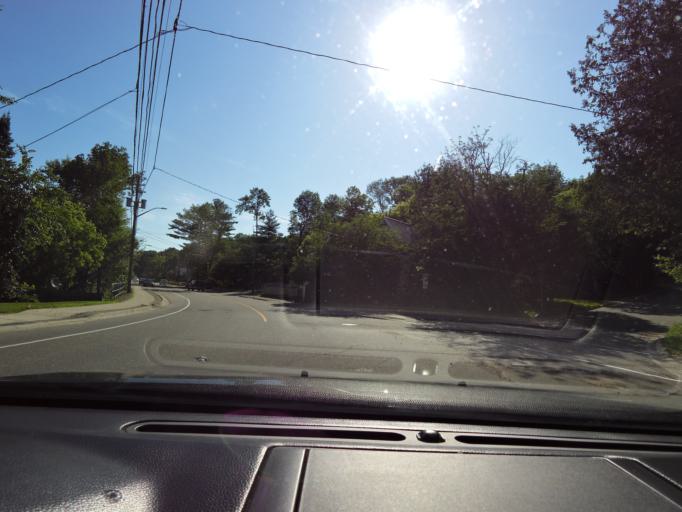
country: CA
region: Ontario
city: Huntsville
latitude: 45.3203
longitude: -79.2303
